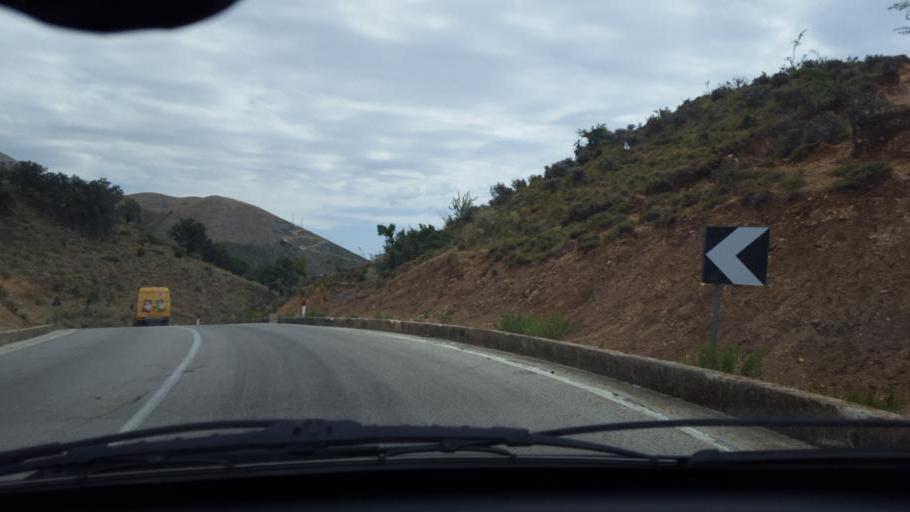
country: AL
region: Vlore
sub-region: Rrethi i Sarandes
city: Lukove
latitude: 40.0417
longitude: 19.8765
